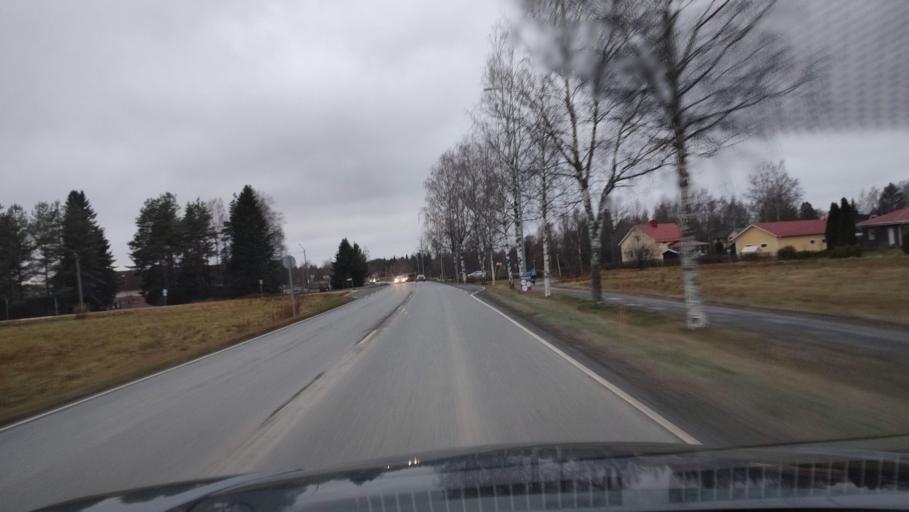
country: FI
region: Southern Ostrobothnia
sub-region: Suupohja
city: Kauhajoki
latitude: 62.4182
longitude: 22.1939
